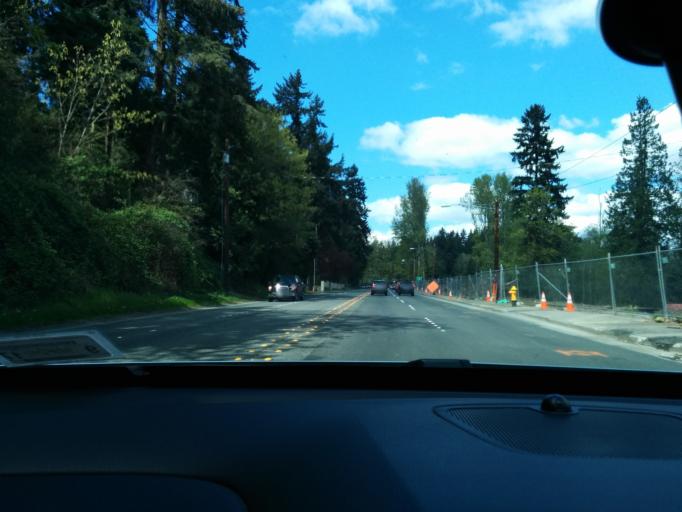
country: US
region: Washington
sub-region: King County
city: Bellevue
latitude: 47.5912
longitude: -122.1934
